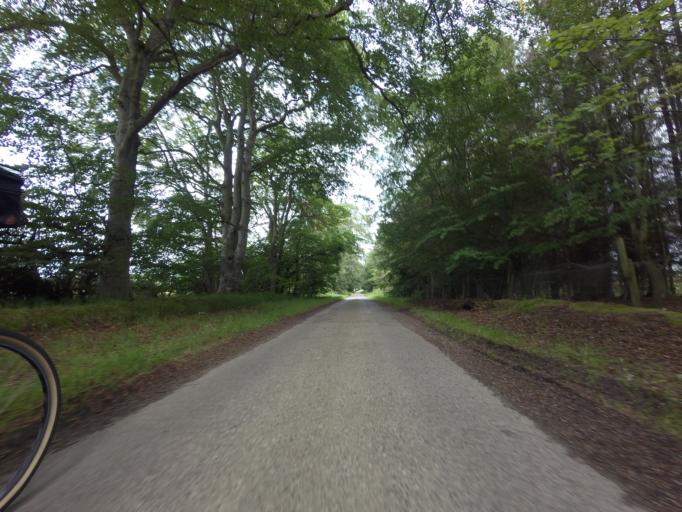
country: GB
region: Scotland
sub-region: Moray
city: Hopeman
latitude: 57.6707
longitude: -3.3977
